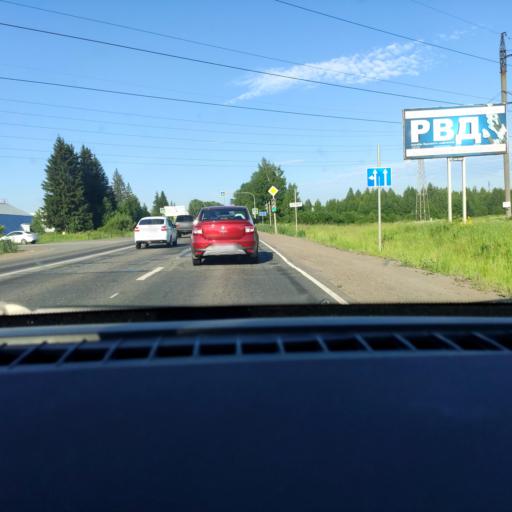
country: RU
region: Udmurtiya
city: Khokhryaki
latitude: 56.9121
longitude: 53.3797
